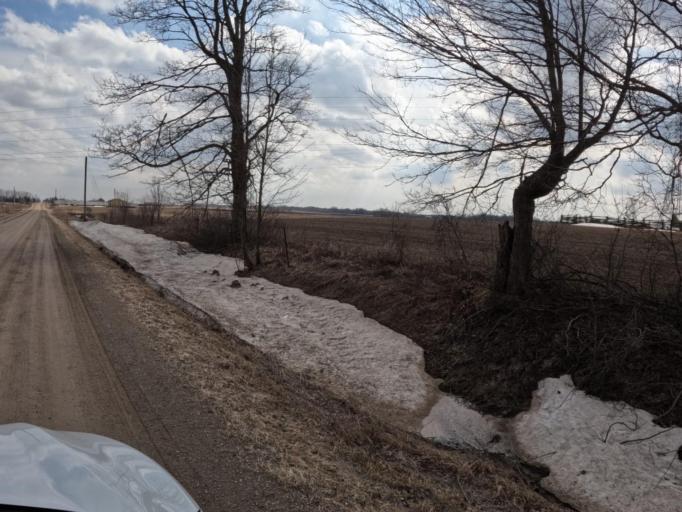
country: CA
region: Ontario
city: Shelburne
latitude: 43.9607
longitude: -80.2991
